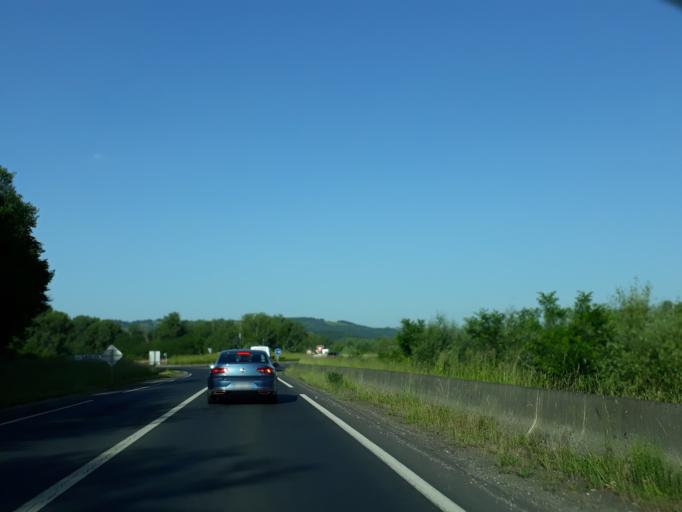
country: FR
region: Limousin
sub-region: Departement de la Correze
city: Saint-Pantaleon-de-Larche
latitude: 45.1288
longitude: 1.4396
